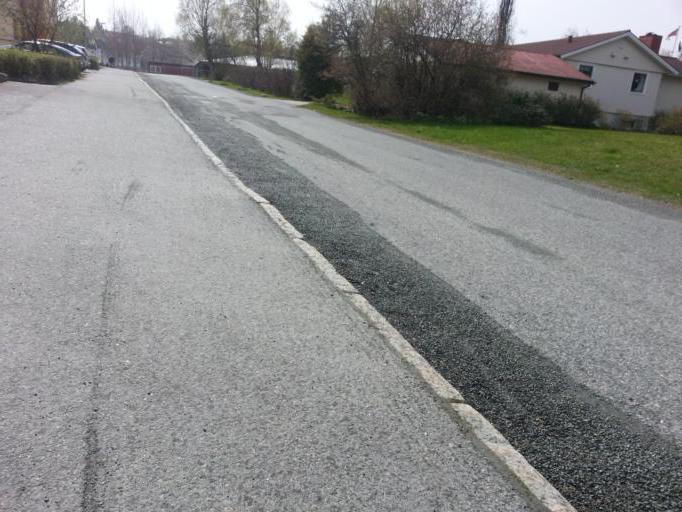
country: NO
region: Sor-Trondelag
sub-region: Trondheim
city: Trondheim
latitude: 63.3959
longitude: 10.3455
